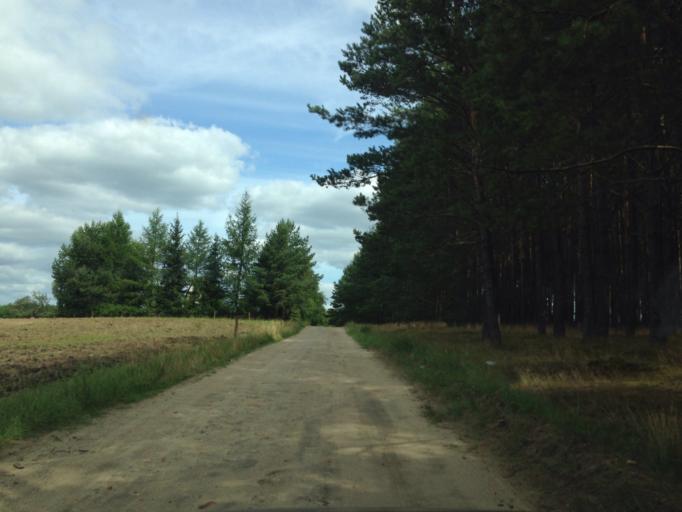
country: PL
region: Pomeranian Voivodeship
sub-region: Powiat bytowski
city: Studzienice
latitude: 54.0697
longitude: 17.6799
